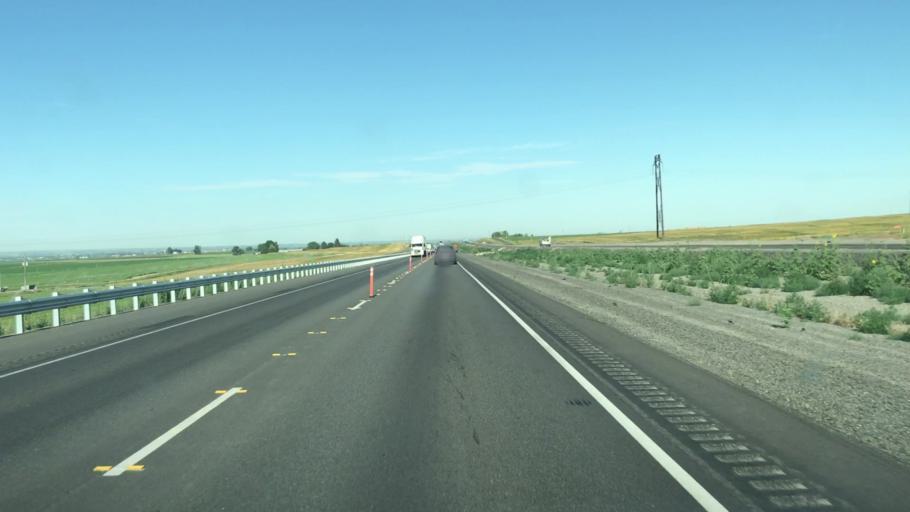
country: US
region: Idaho
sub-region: Twin Falls County
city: Hansen
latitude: 42.5761
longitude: -114.2358
